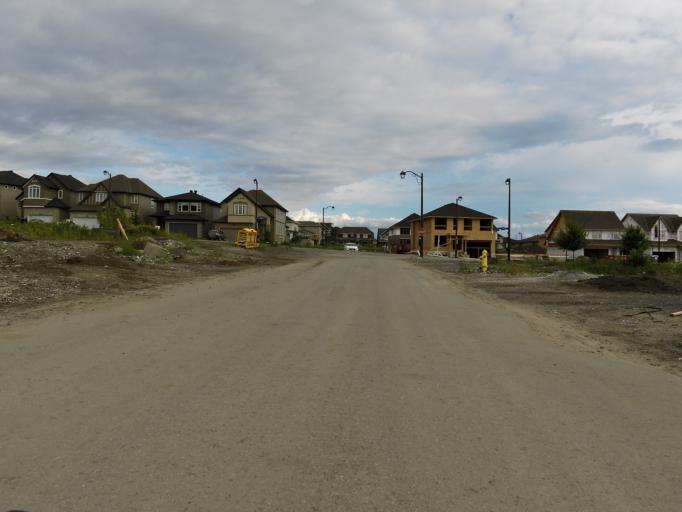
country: CA
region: Ontario
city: Bells Corners
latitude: 45.3189
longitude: -75.9440
